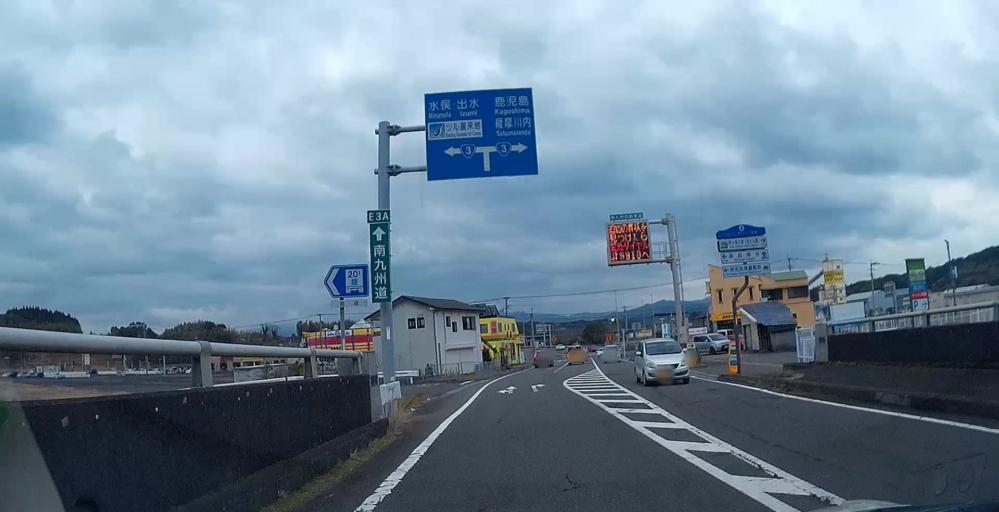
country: JP
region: Kagoshima
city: Akune
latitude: 32.0626
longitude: 130.2259
